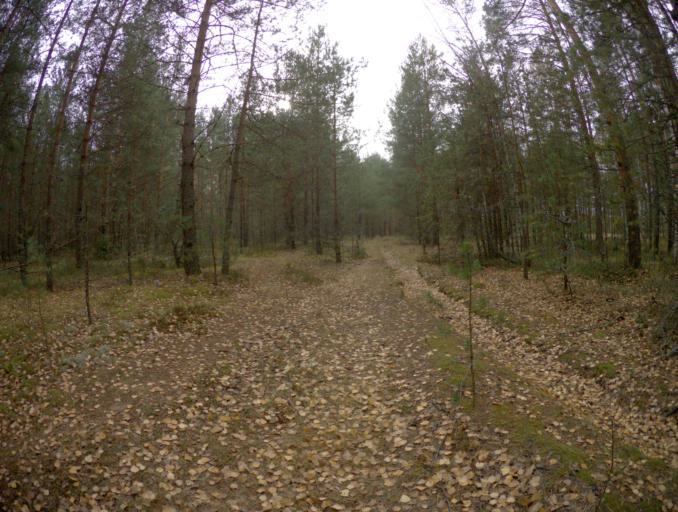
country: RU
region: Vladimir
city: Kommunar
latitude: 56.1038
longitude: 40.4607
